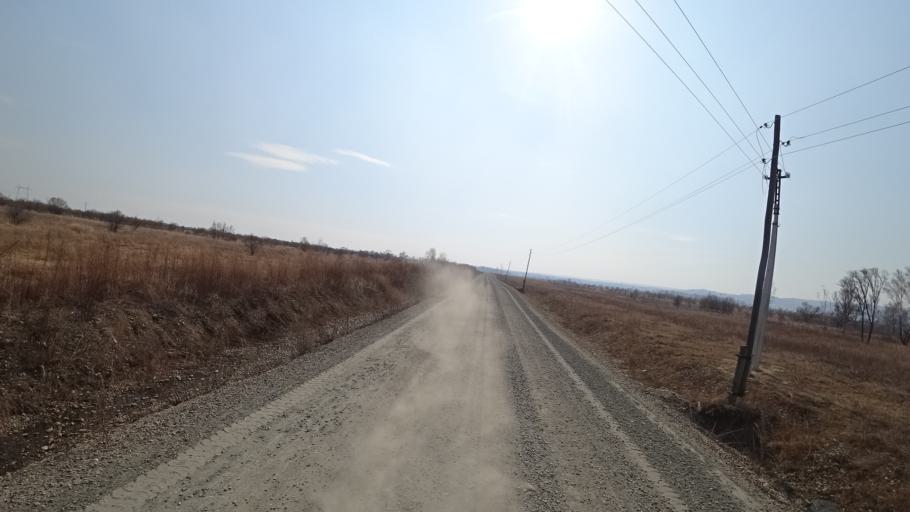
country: RU
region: Amur
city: Novobureyskiy
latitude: 49.8140
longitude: 129.9736
